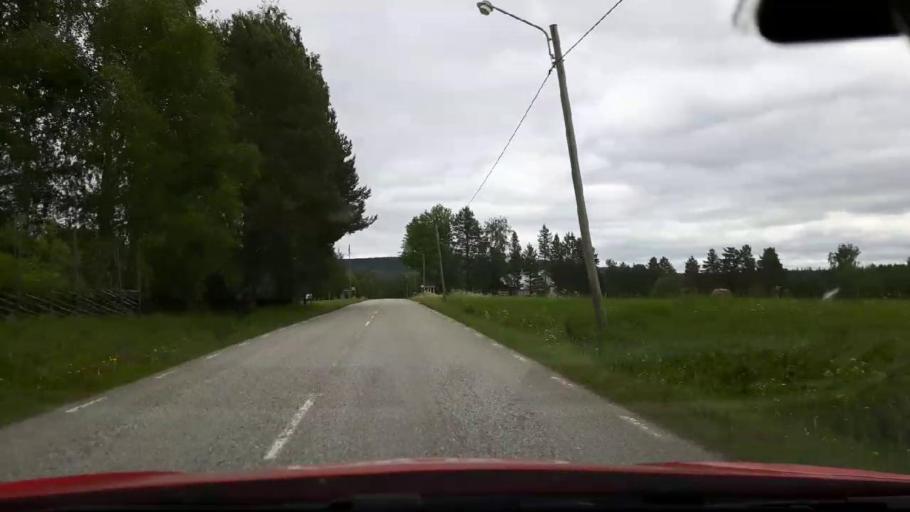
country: SE
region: Jaemtland
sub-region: Ragunda Kommun
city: Hammarstrand
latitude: 63.2169
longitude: 15.9437
